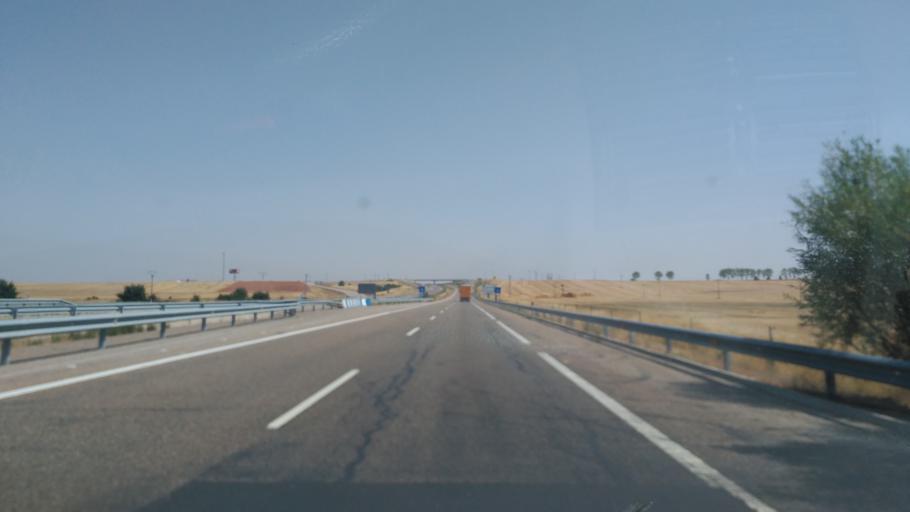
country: ES
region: Castille and Leon
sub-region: Provincia de Salamanca
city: Robliza de Cojos
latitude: 40.8711
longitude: -5.9921
